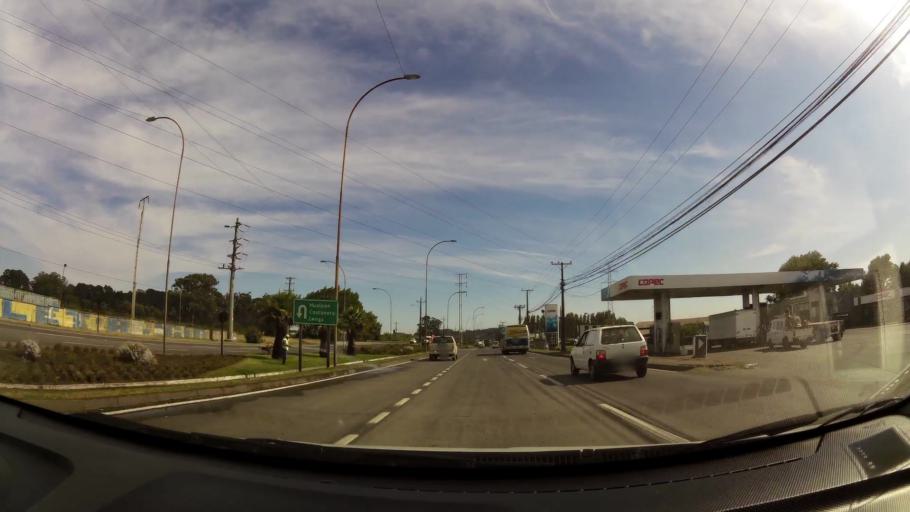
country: CL
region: Biobio
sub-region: Provincia de Concepcion
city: Talcahuano
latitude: -36.7729
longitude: -73.1139
